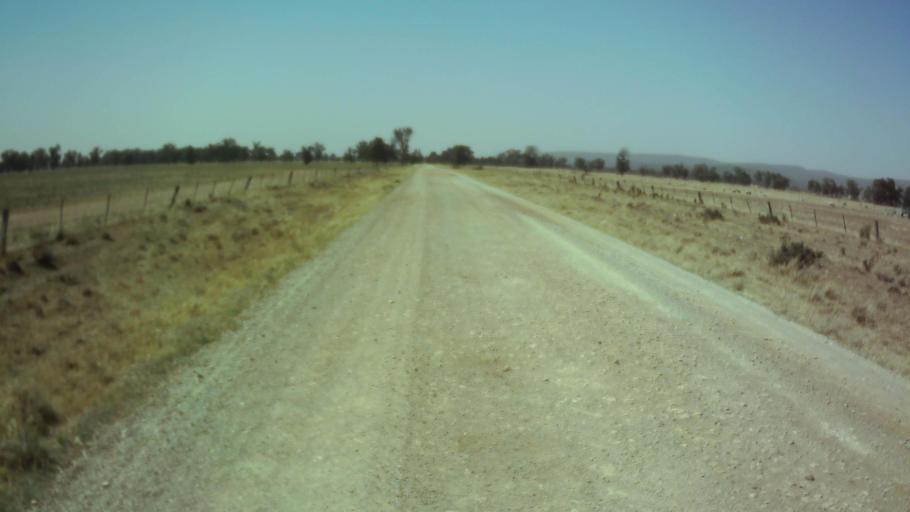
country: AU
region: New South Wales
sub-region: Weddin
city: Grenfell
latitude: -34.0291
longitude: 147.9128
